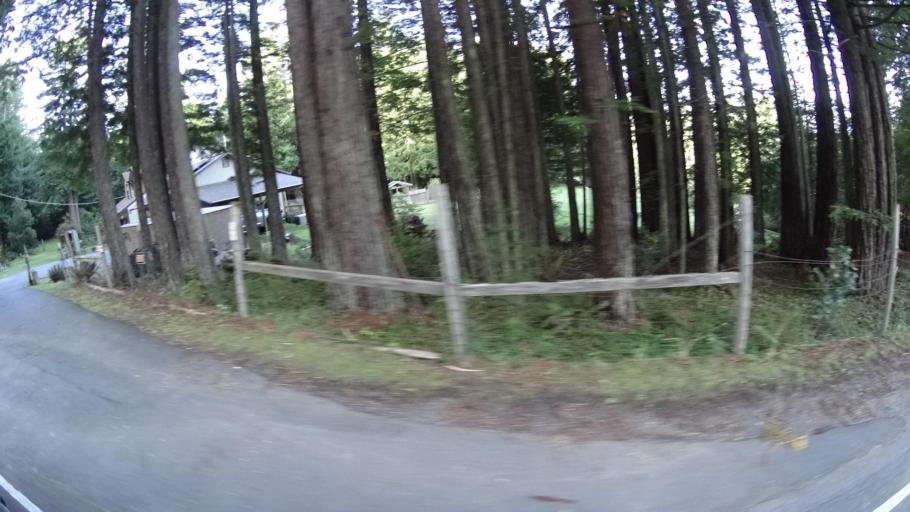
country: US
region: California
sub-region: Humboldt County
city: Bayside
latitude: 40.7642
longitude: -123.9976
